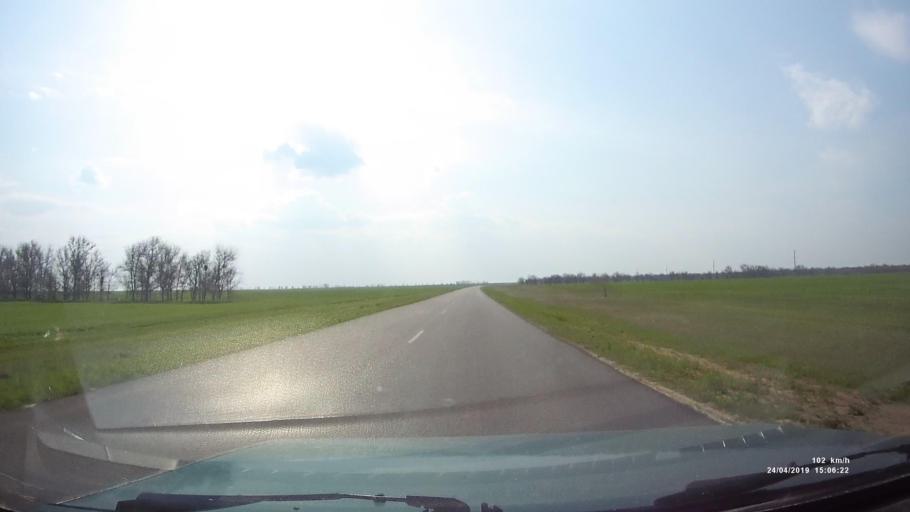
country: RU
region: Rostov
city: Remontnoye
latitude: 46.5589
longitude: 43.4288
